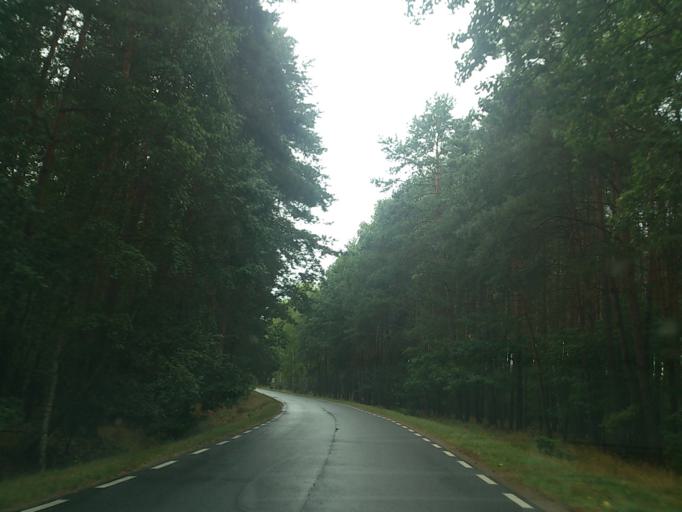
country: PL
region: Greater Poland Voivodeship
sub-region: Powiat poznanski
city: Pobiedziska
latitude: 52.5144
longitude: 17.1983
